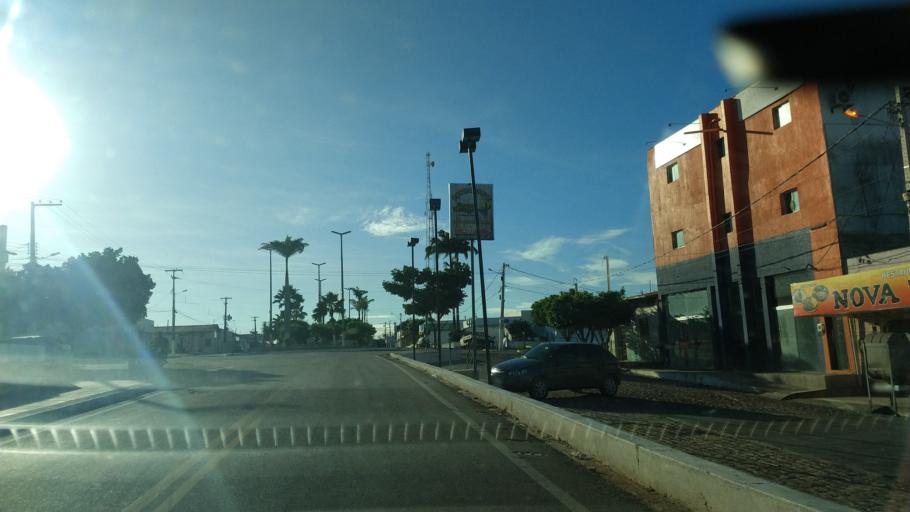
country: BR
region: Rio Grande do Norte
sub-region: Tangara
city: Tangara
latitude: -6.2010
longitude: -35.8000
